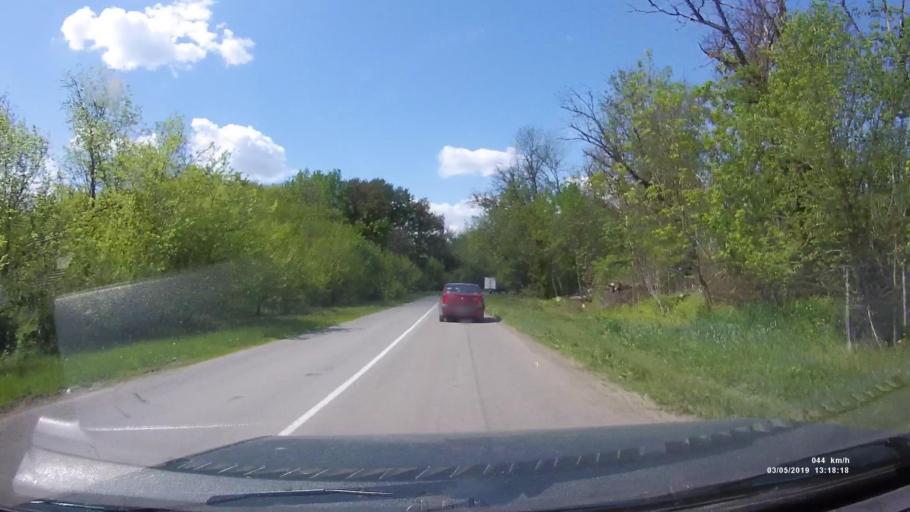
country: RU
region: Rostov
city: Semikarakorsk
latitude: 47.5320
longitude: 40.7490
